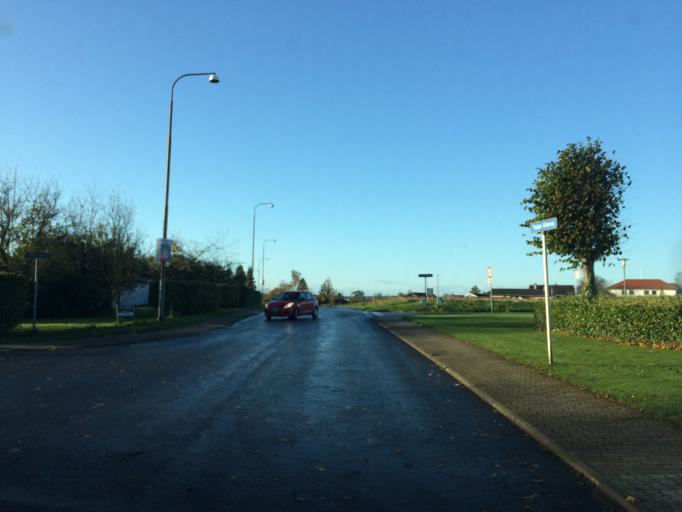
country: DK
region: South Denmark
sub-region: Fredericia Kommune
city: Taulov
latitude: 55.5390
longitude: 9.6090
